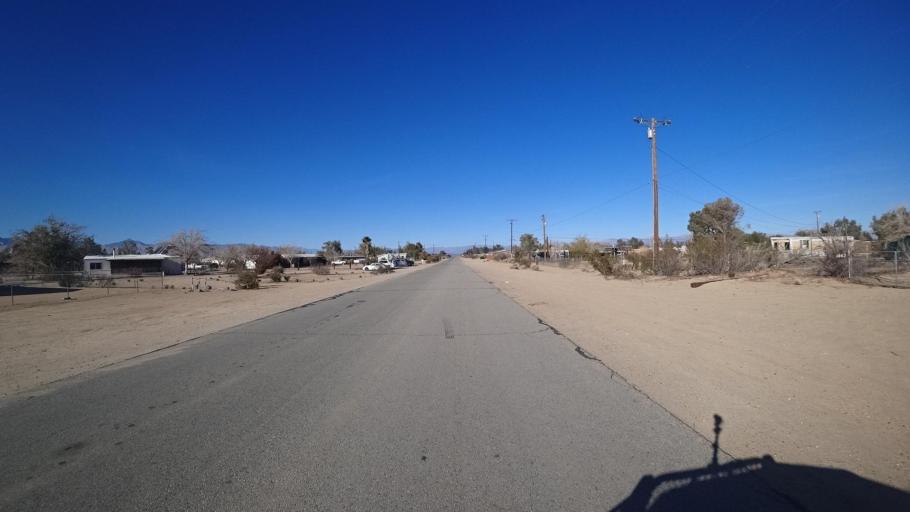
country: US
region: California
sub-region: Kern County
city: China Lake Acres
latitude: 35.6400
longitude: -117.7586
